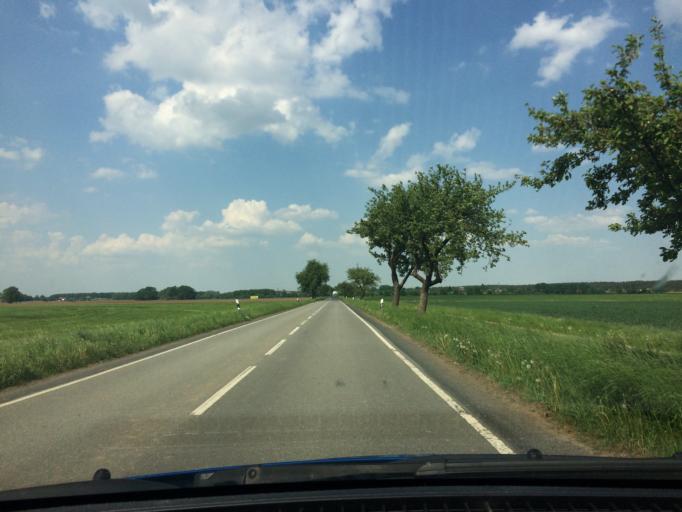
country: DE
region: Lower Saxony
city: Neu Darchau
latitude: 53.2663
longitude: 10.9219
